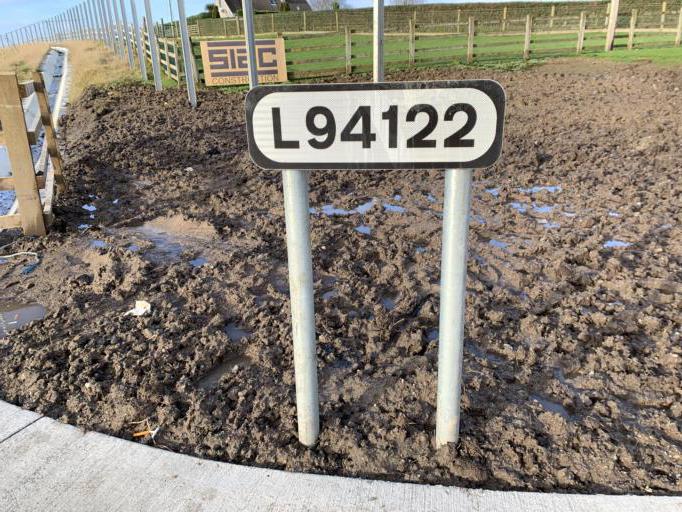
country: IE
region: Connaught
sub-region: Sligo
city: Sligo
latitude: 54.2605
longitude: -8.4850
